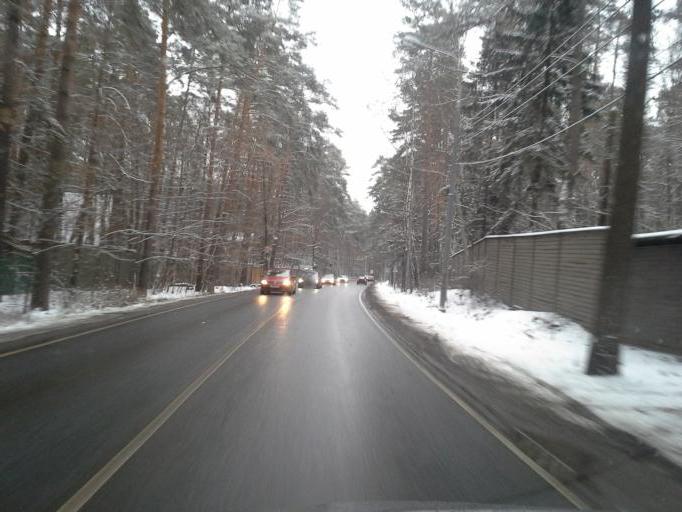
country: RU
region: Moskovskaya
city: Nikolina Gora
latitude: 55.7348
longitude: 37.0381
